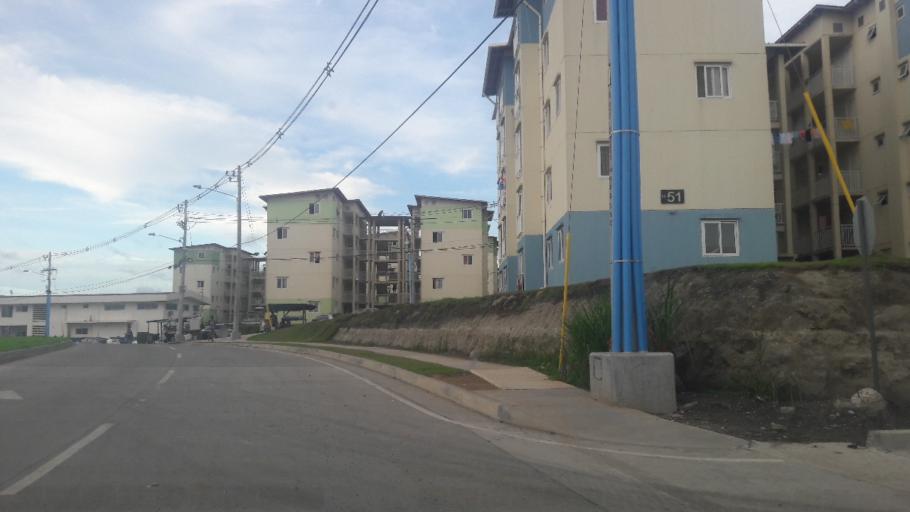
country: PA
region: Colon
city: Cativa
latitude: 9.3697
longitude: -79.8511
